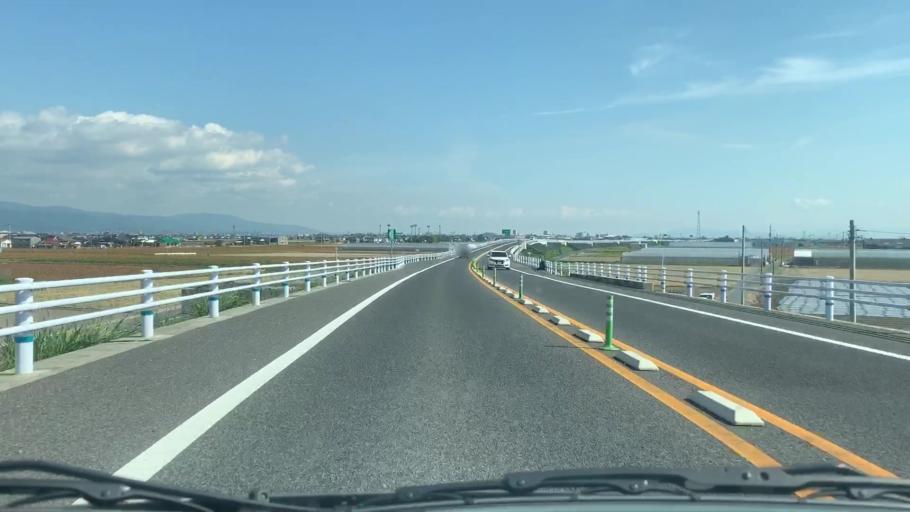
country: JP
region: Saga Prefecture
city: Saga-shi
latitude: 33.2292
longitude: 130.2228
